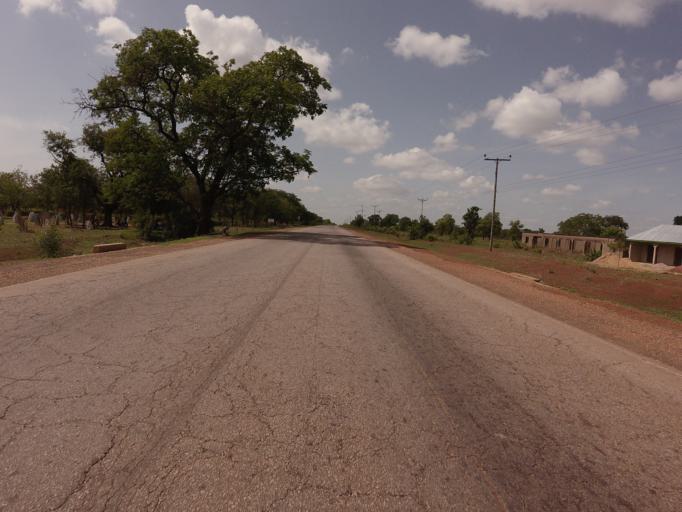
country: GH
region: Northern
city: Savelugu
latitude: 9.8787
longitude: -0.8709
